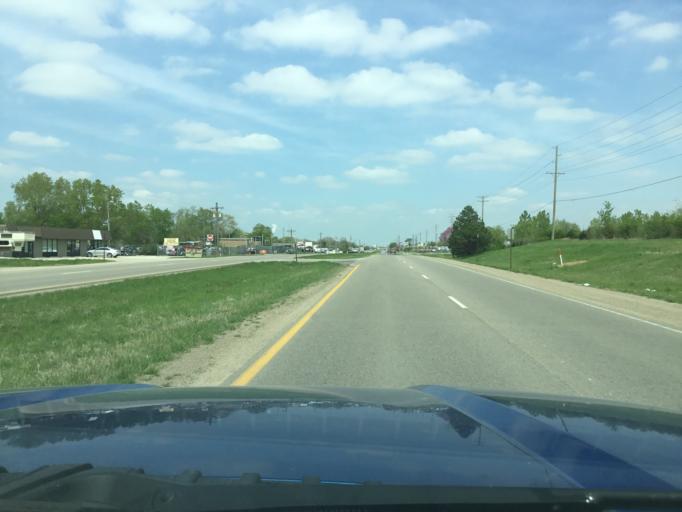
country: US
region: Kansas
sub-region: Shawnee County
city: Topeka
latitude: 38.9737
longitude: -95.6876
